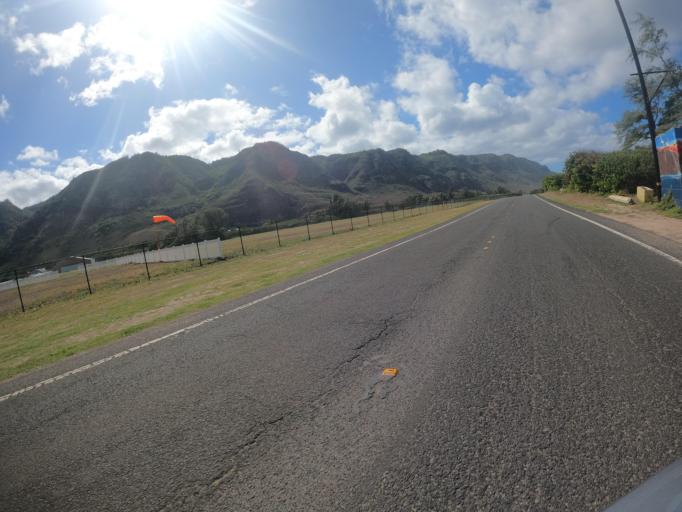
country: US
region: Hawaii
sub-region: Honolulu County
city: Mokuleia
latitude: 21.5823
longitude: -158.2097
